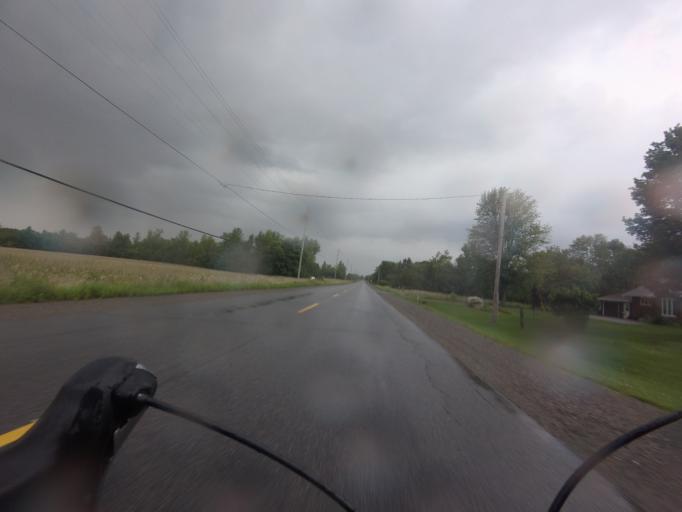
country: CA
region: Ontario
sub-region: Lanark County
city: Smiths Falls
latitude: 44.9276
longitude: -75.8351
